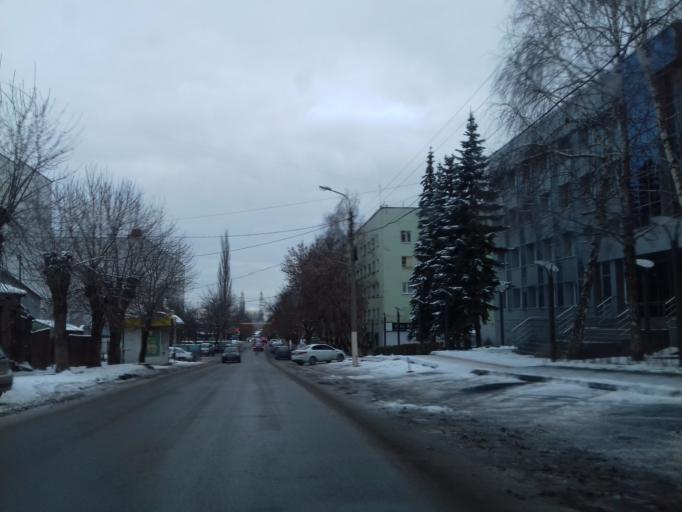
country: RU
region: Bashkortostan
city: Ufa
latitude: 54.7267
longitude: 55.9703
